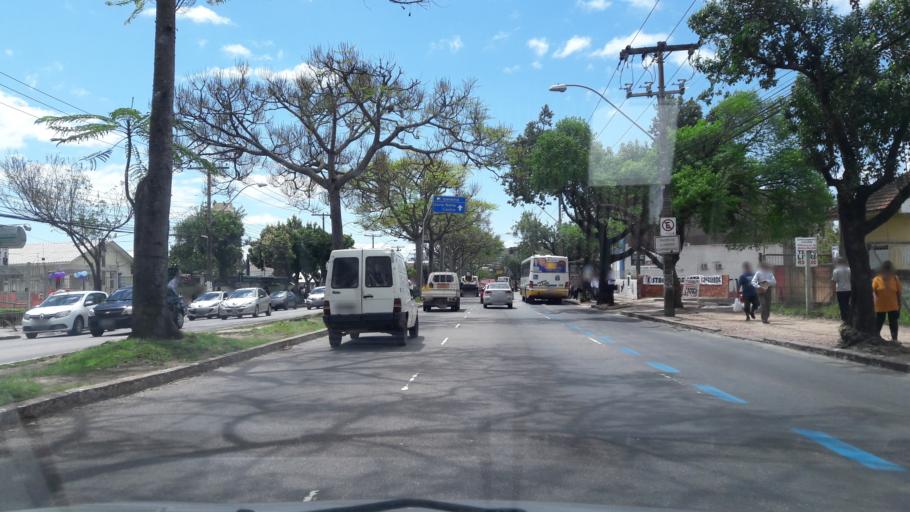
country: BR
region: Rio Grande do Sul
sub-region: Porto Alegre
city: Porto Alegre
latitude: -30.1015
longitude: -51.2311
